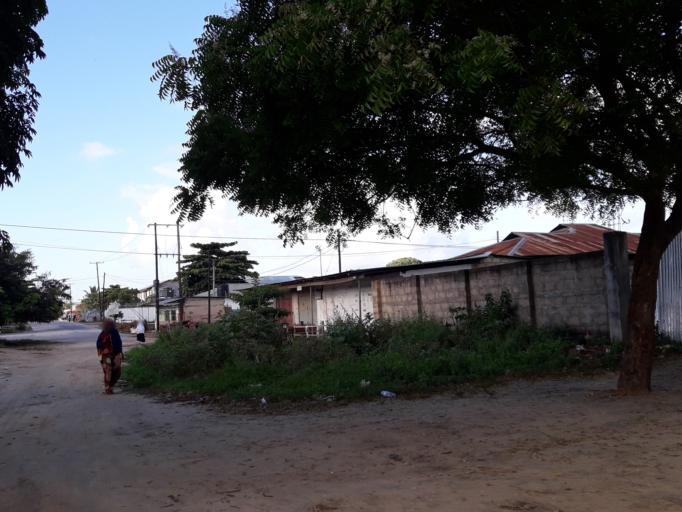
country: TZ
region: Zanzibar Urban/West
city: Zanzibar
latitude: -6.1809
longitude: 39.2273
